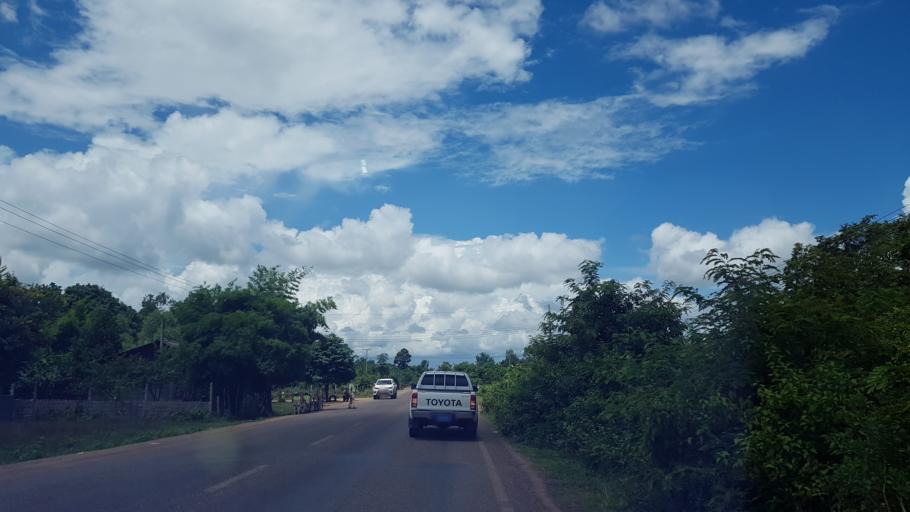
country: LA
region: Vientiane
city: Vientiane
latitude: 18.1131
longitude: 102.5856
